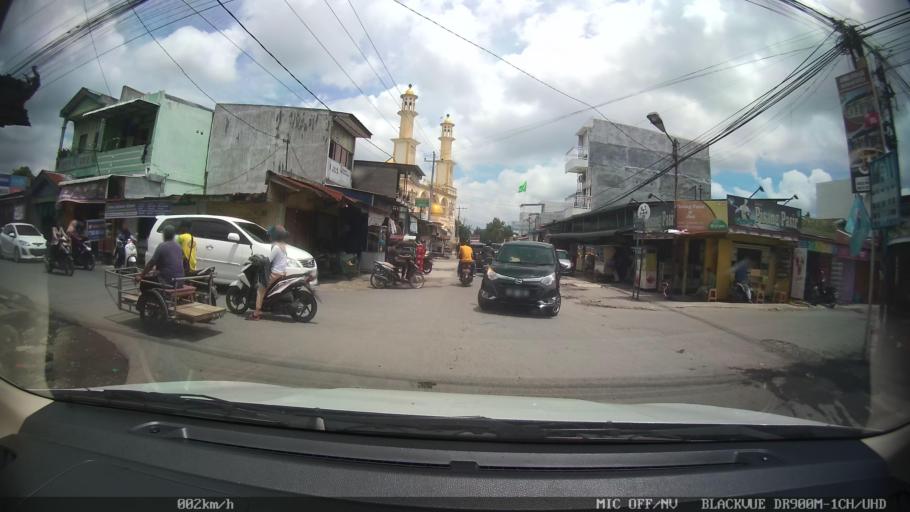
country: ID
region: North Sumatra
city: Medan
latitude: 3.6201
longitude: 98.7483
